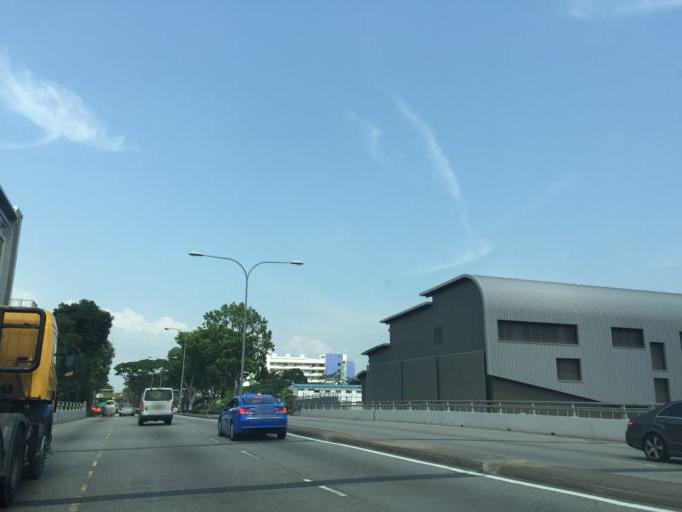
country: SG
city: Singapore
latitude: 1.3417
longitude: 103.9469
